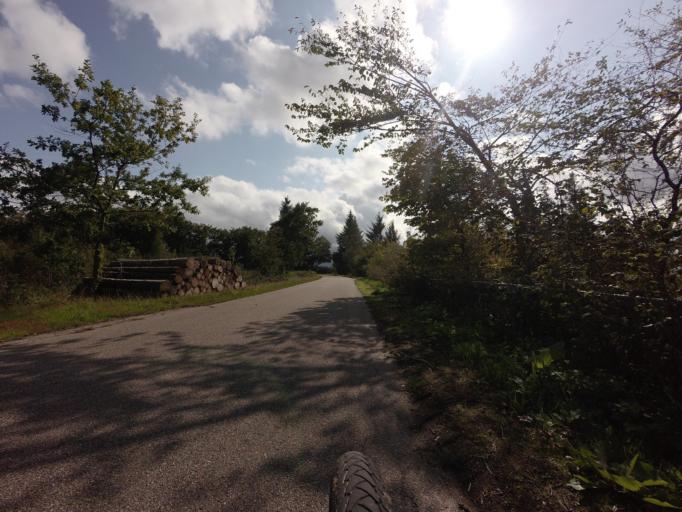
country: DK
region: North Denmark
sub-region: Hjorring Kommune
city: Hirtshals
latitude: 57.5442
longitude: 10.0568
